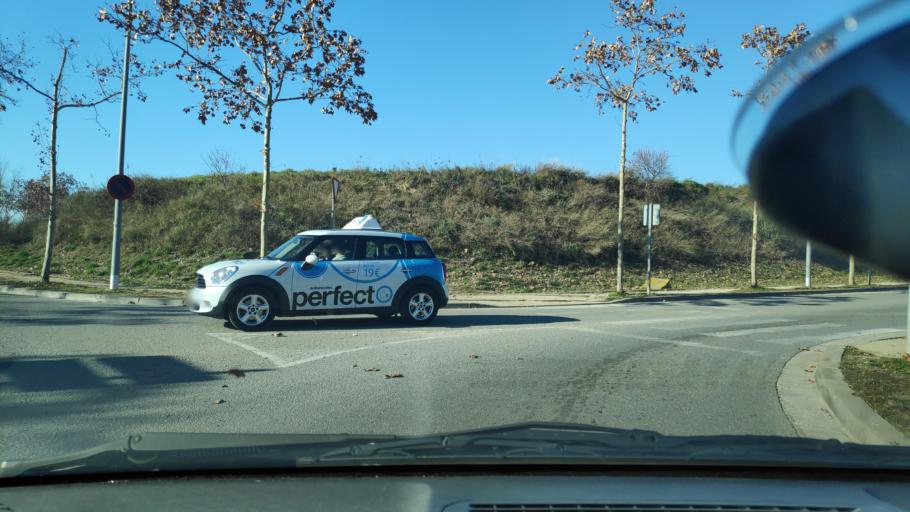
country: ES
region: Catalonia
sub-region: Provincia de Barcelona
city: Sant Quirze del Valles
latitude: 41.5504
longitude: 2.0789
